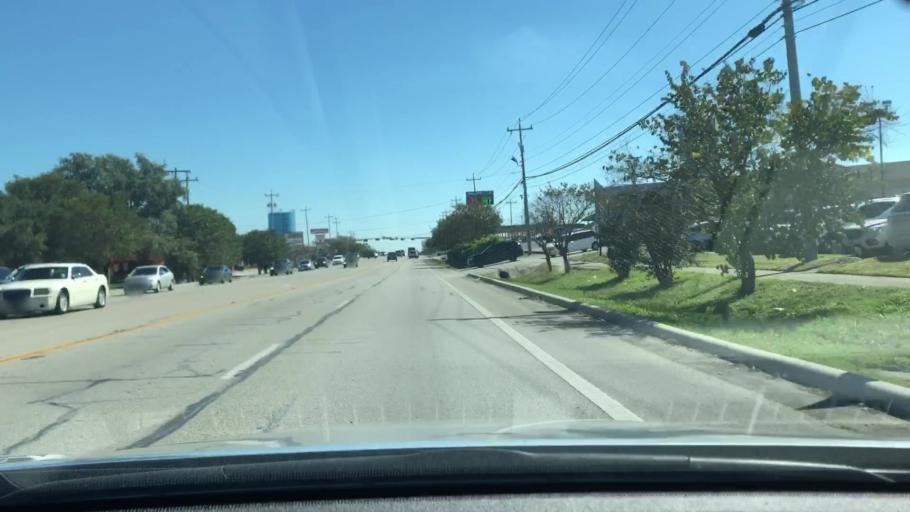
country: US
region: Texas
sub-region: Bexar County
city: Live Oak
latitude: 29.5592
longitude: -98.3242
